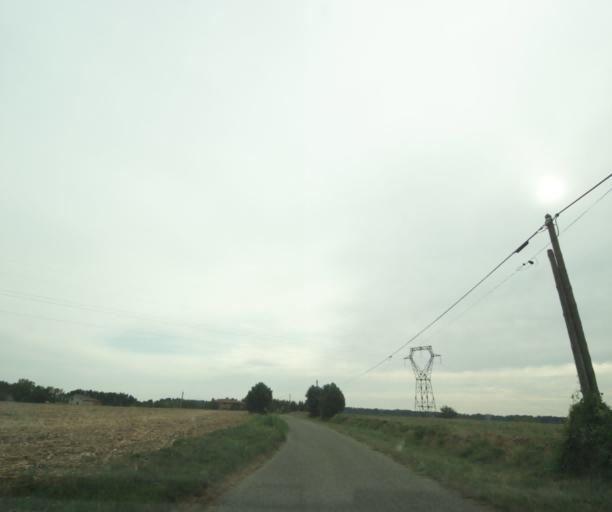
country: FR
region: Midi-Pyrenees
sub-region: Departement du Tarn-et-Garonne
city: Saint-Porquier
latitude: 43.9765
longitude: 1.1855
